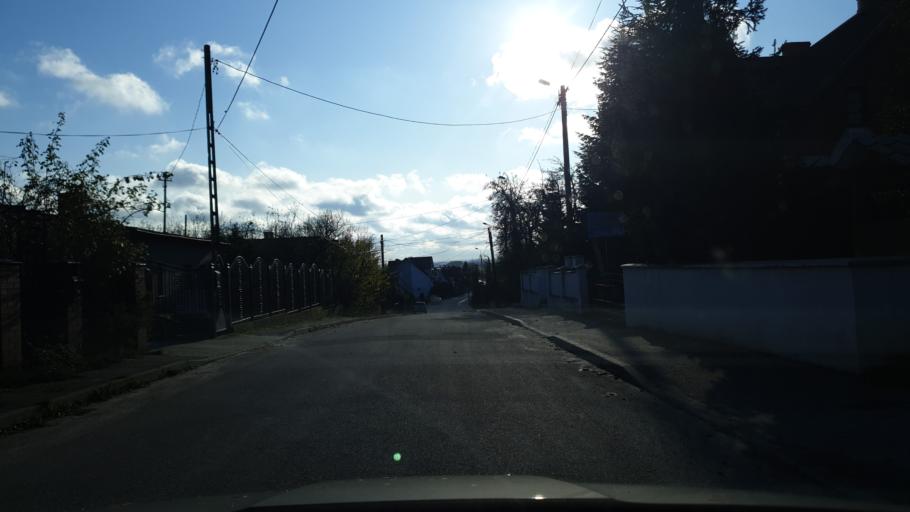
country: PL
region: Pomeranian Voivodeship
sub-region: Powiat pucki
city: Gniezdzewo
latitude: 54.7570
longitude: 18.3987
